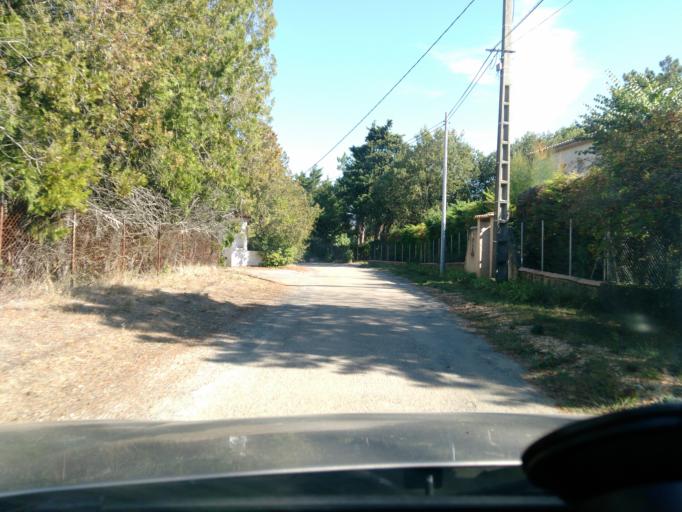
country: FR
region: Rhone-Alpes
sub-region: Departement de la Drome
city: Montboucher-sur-Jabron
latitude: 44.5567
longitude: 4.7908
